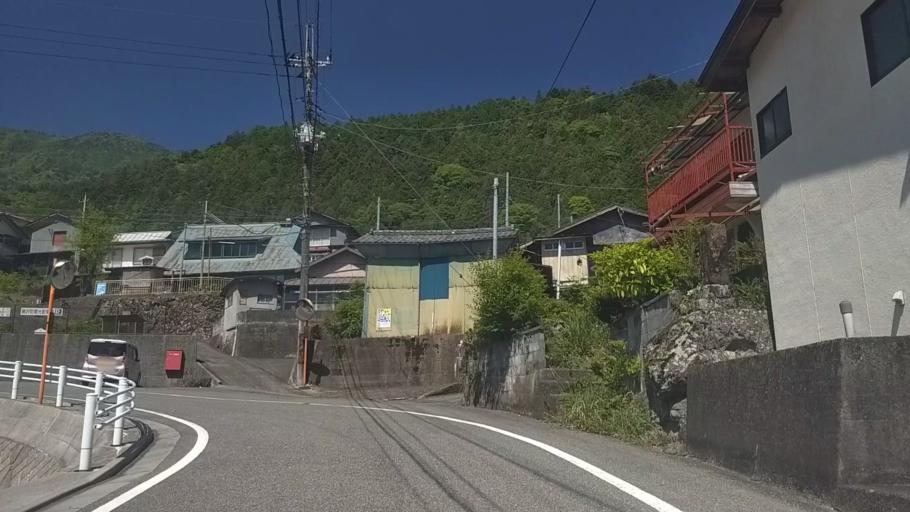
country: JP
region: Yamanashi
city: Ryuo
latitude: 35.5070
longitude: 138.3966
